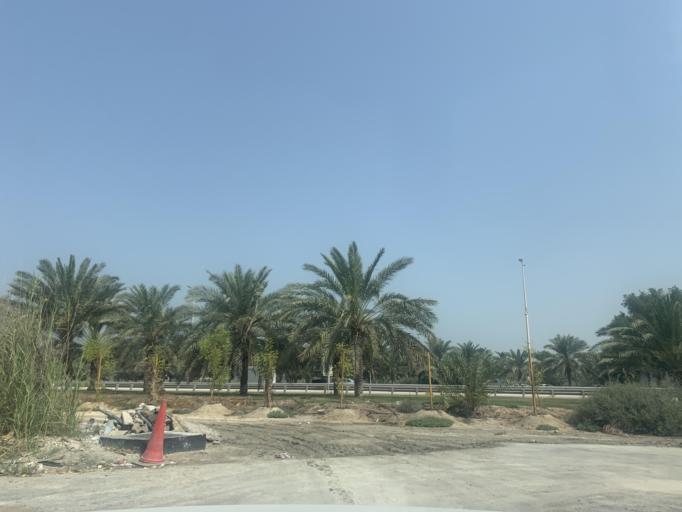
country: BH
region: Central Governorate
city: Madinat Hamad
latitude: 26.1717
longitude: 50.4563
